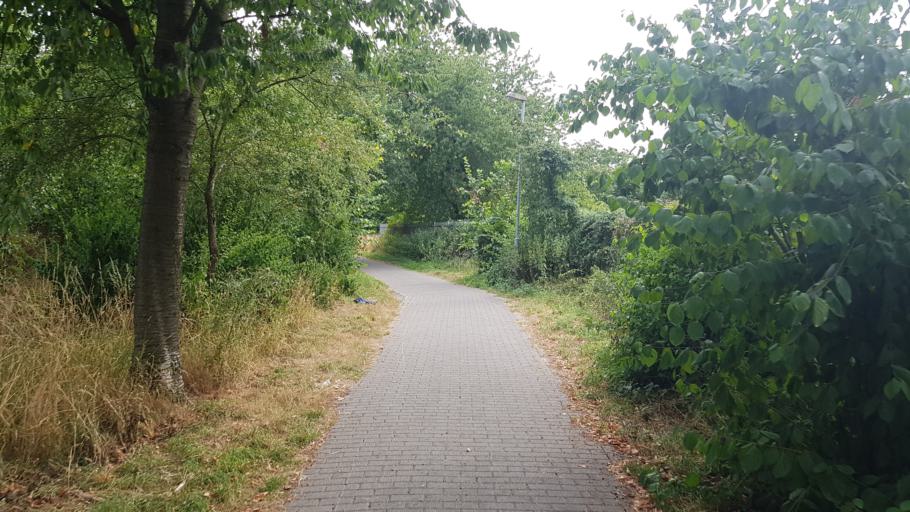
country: DE
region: North Rhine-Westphalia
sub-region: Regierungsbezirk Dusseldorf
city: Kamp-Lintfort
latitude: 51.4598
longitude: 6.5711
